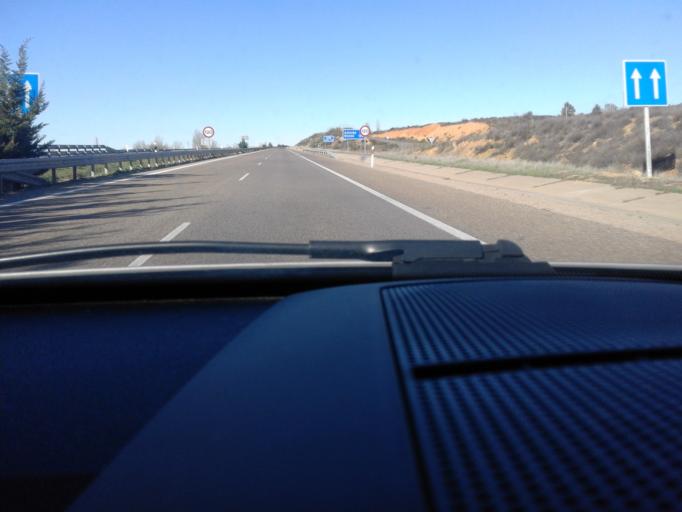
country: ES
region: Castille and Leon
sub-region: Provincia de Leon
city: Onzonilla
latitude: 42.5362
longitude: -5.6061
